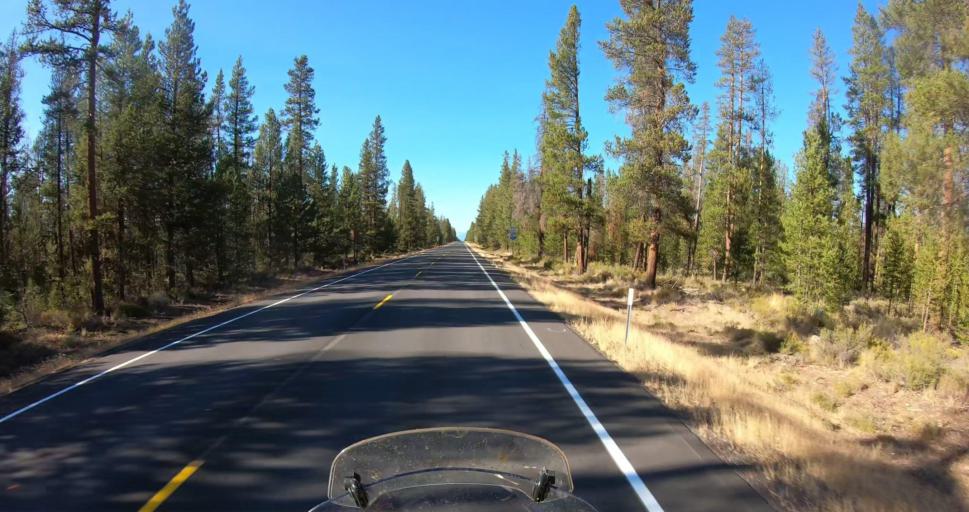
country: US
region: Oregon
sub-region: Deschutes County
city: La Pine
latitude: 43.5155
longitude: -121.4531
